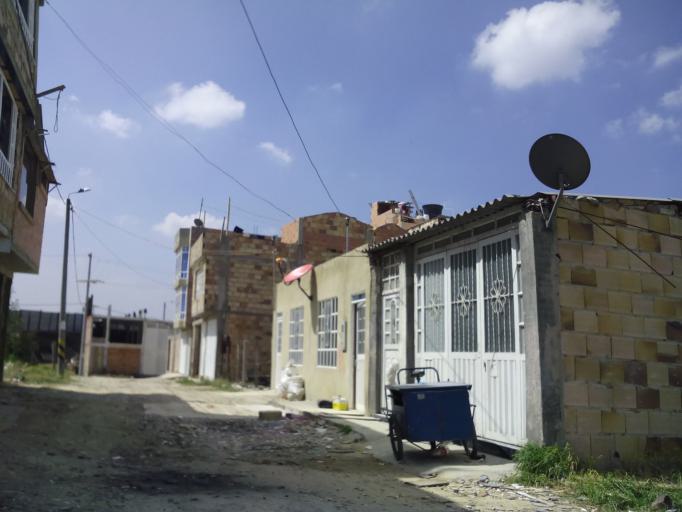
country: CO
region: Bogota D.C.
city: Bogota
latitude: 4.6608
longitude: -74.1426
